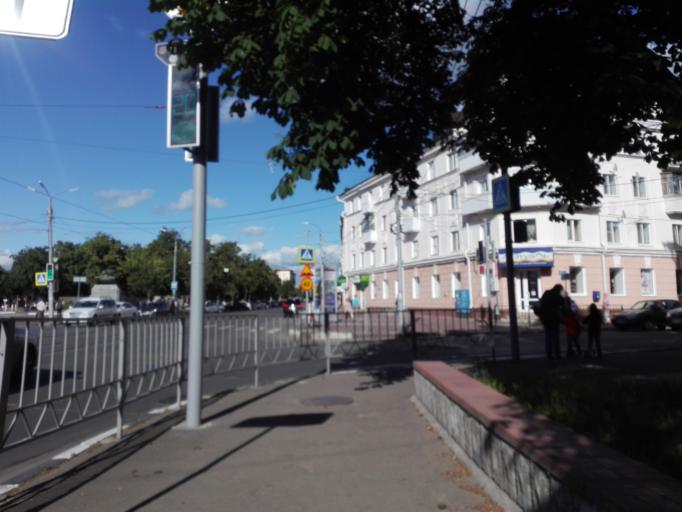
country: RU
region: Orjol
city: Orel
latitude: 52.9671
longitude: 36.0756
